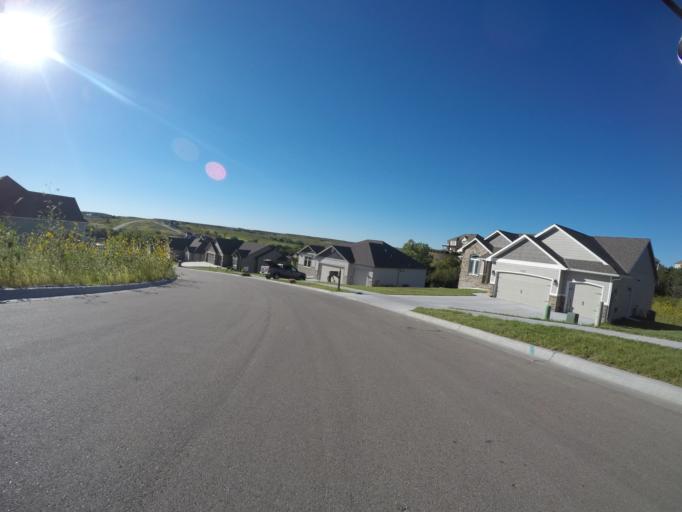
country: US
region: Kansas
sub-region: Riley County
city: Manhattan
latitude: 39.2103
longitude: -96.6299
